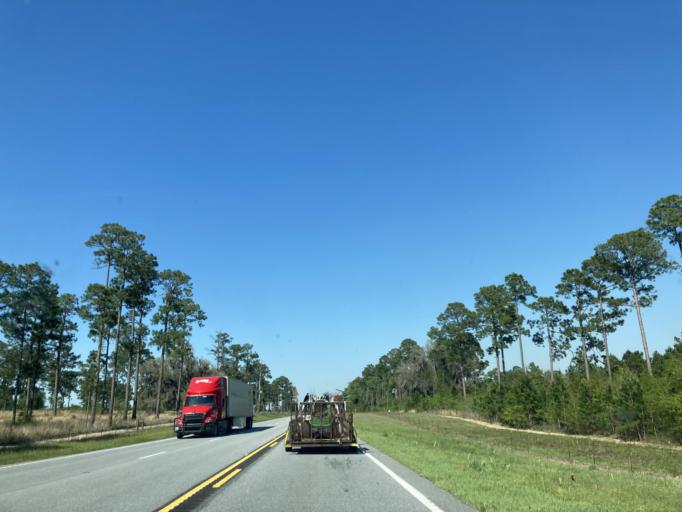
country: US
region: Georgia
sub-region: Dougherty County
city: Putney
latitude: 31.4490
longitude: -84.2625
